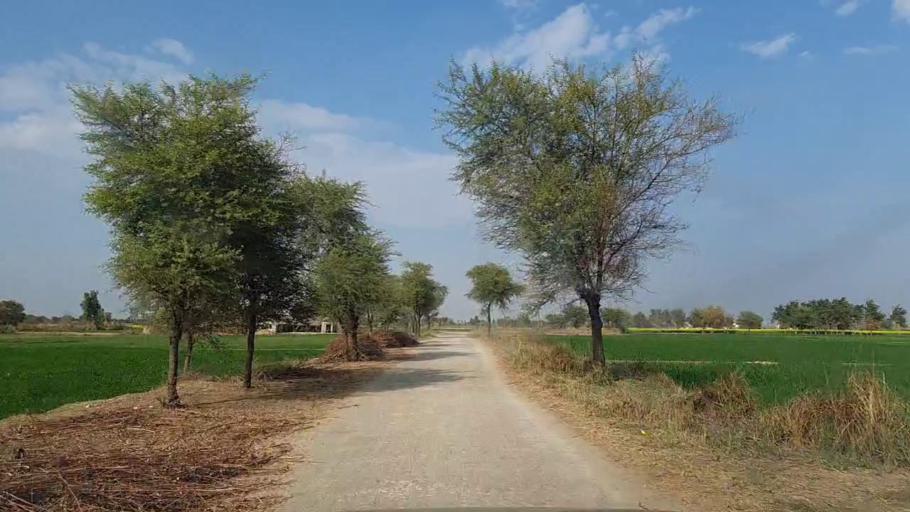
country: PK
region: Sindh
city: Sanghar
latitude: 26.2375
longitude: 69.0195
